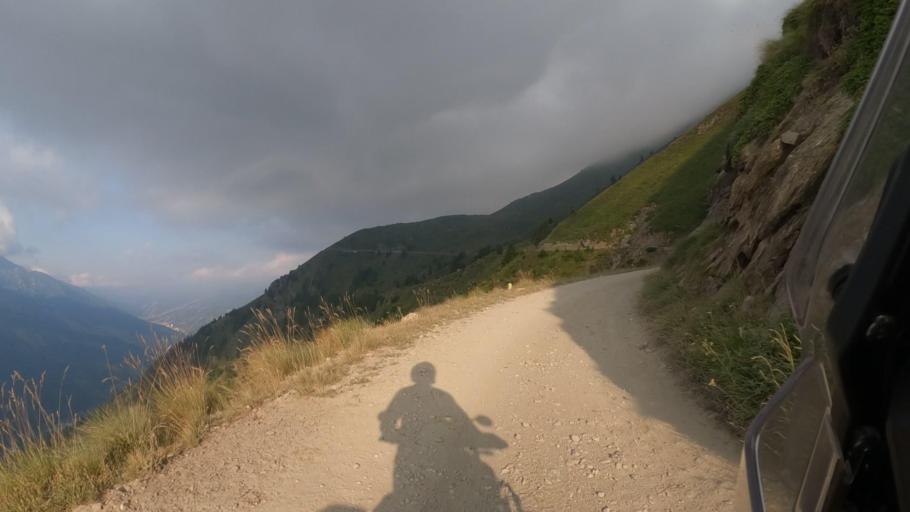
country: IT
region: Piedmont
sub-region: Provincia di Torino
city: Usseaux
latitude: 45.0625
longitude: 7.0143
